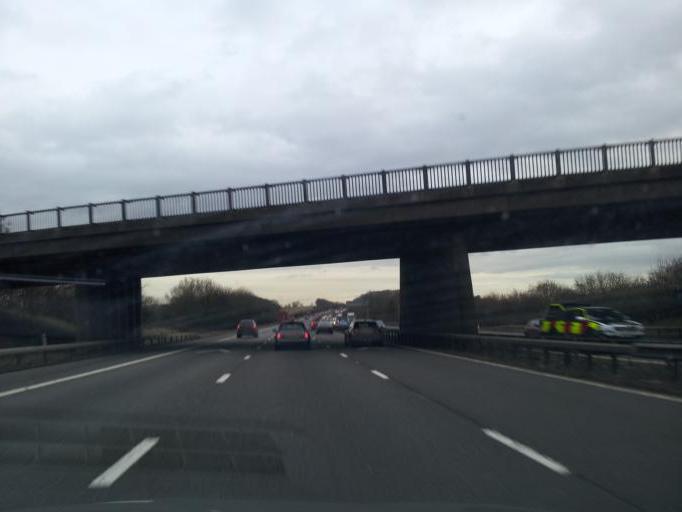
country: GB
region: England
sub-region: Warwickshire
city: Long Lawford
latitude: 52.4317
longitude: -1.3326
